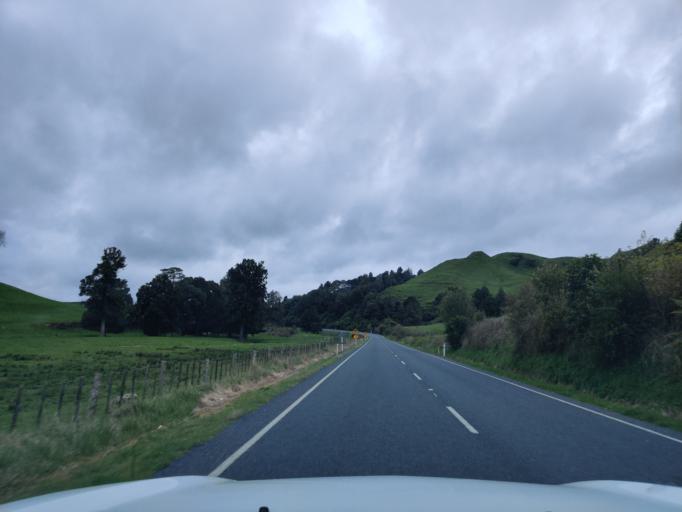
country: NZ
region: Waikato
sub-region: Otorohanga District
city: Otorohanga
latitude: -38.5452
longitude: 175.1843
